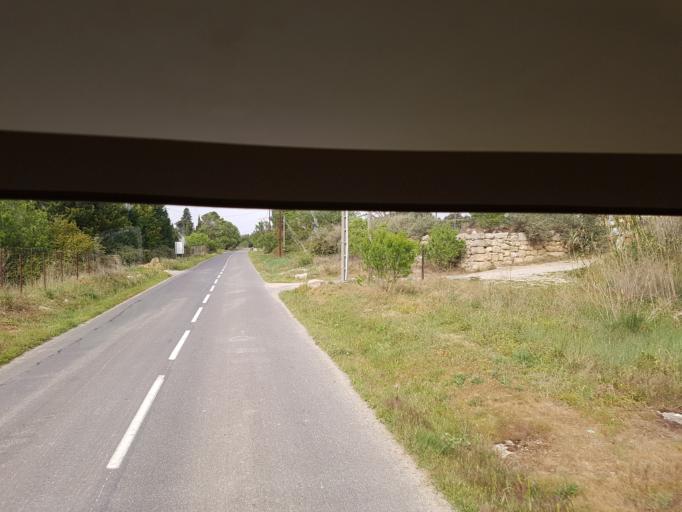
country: FR
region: Languedoc-Roussillon
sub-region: Departement de l'Herault
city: Lespignan
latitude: 43.2625
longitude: 3.1624
